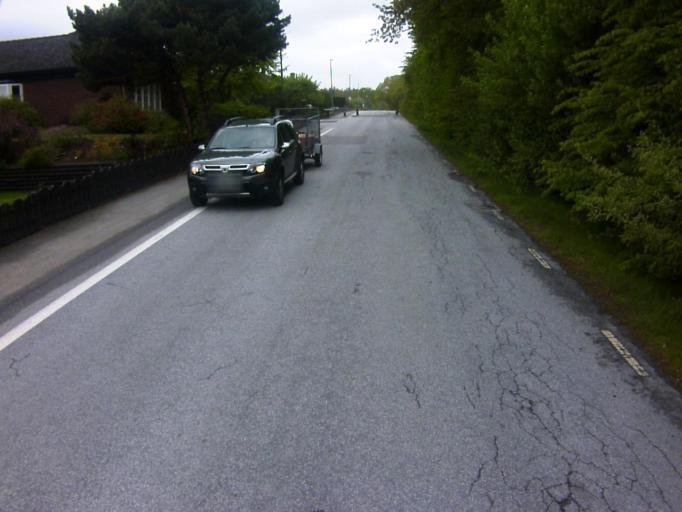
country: SE
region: Blekinge
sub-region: Solvesborgs Kommun
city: Soelvesborg
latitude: 56.0628
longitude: 14.5861
